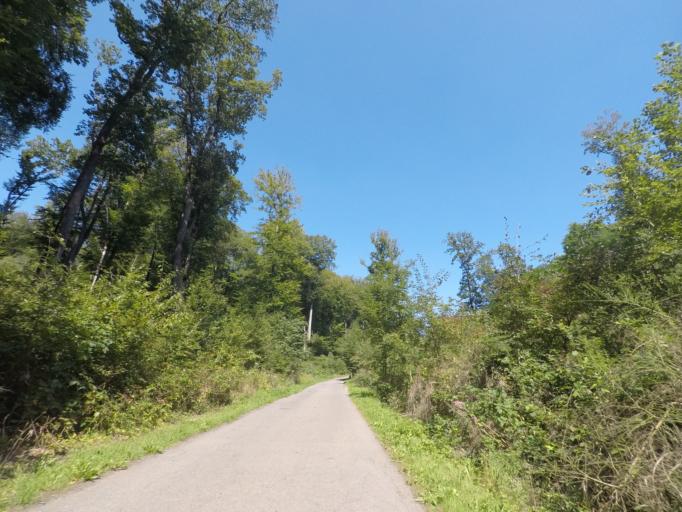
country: LU
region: Luxembourg
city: Bereldange
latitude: 49.6425
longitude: 6.1139
